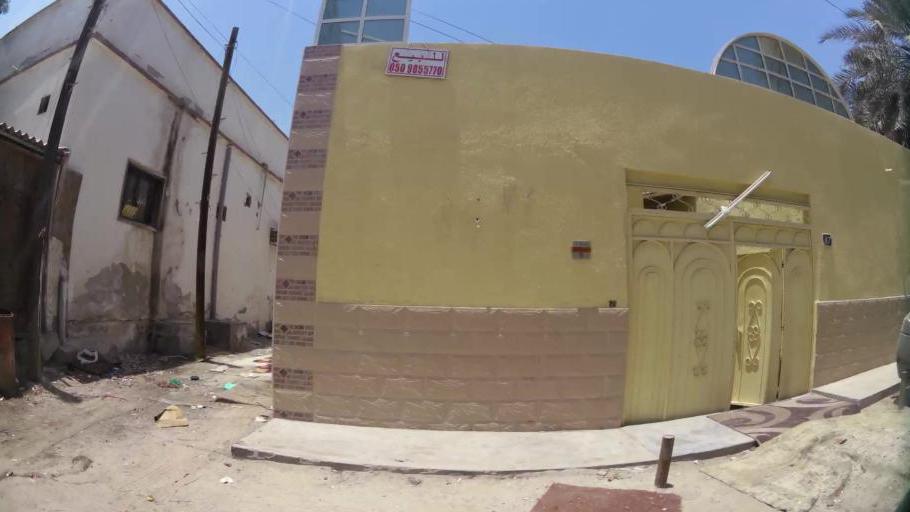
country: AE
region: Ajman
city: Ajman
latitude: 25.3972
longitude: 55.4386
